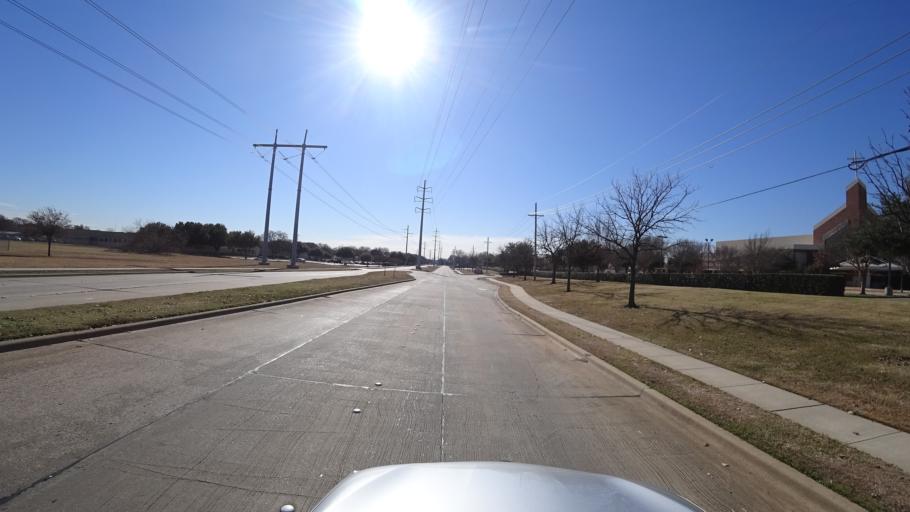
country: US
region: Texas
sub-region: Denton County
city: Lewisville
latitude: 33.0273
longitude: -97.0106
